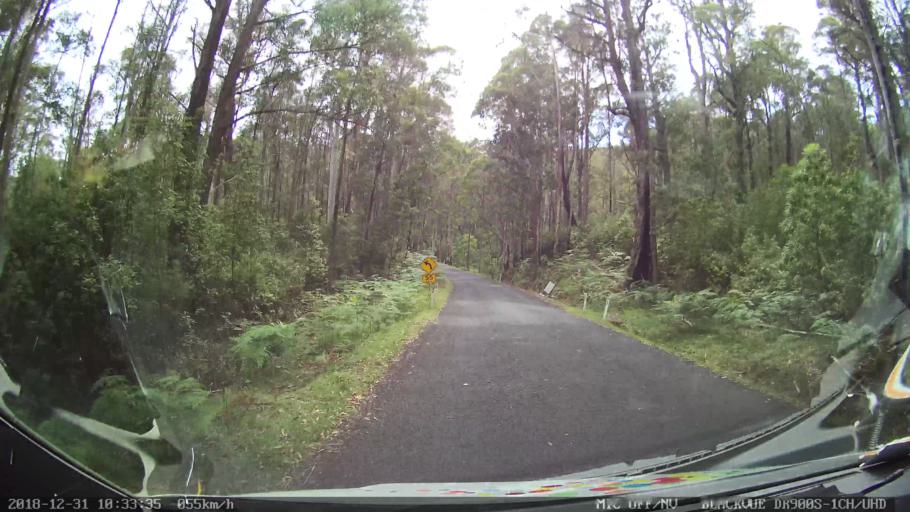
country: AU
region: New South Wales
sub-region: Snowy River
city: Jindabyne
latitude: -36.4461
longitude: 148.1652
